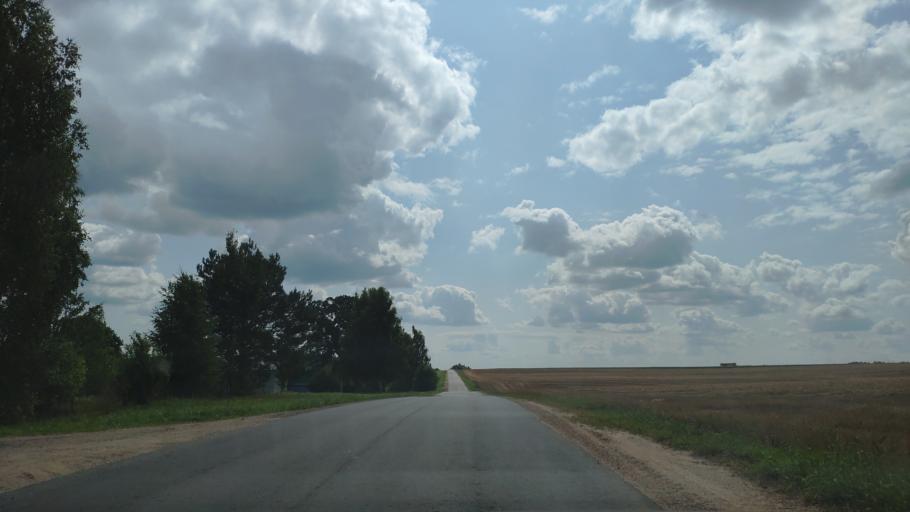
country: BY
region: Minsk
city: Khatsyezhyna
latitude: 53.8387
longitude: 27.3097
